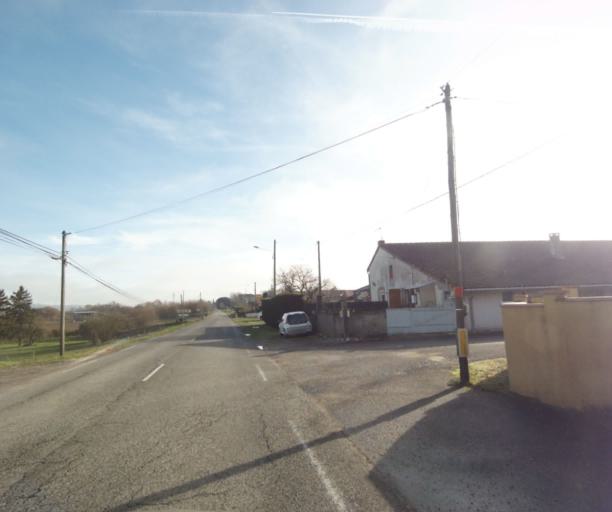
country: FR
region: Midi-Pyrenees
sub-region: Departement de la Haute-Garonne
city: Villemur-sur-Tarn
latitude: 43.8672
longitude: 1.4714
